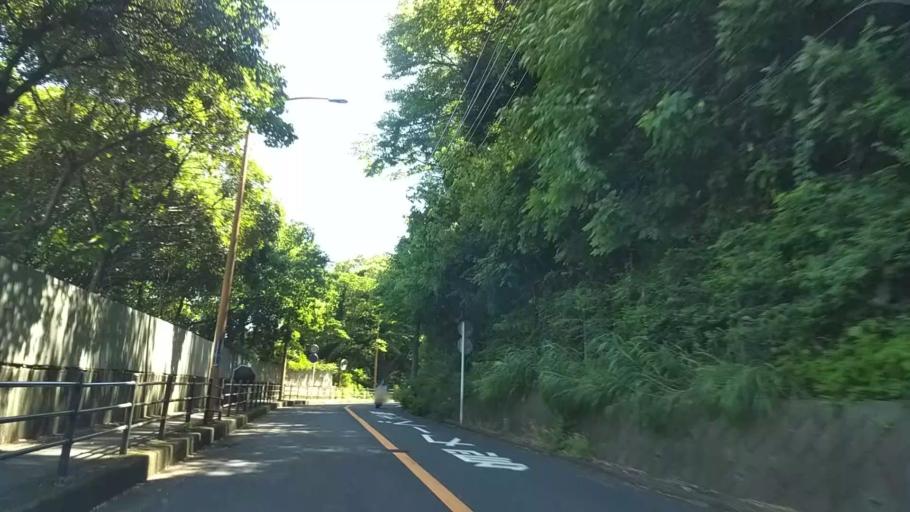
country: JP
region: Kanagawa
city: Zushi
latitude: 35.2947
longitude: 139.5910
